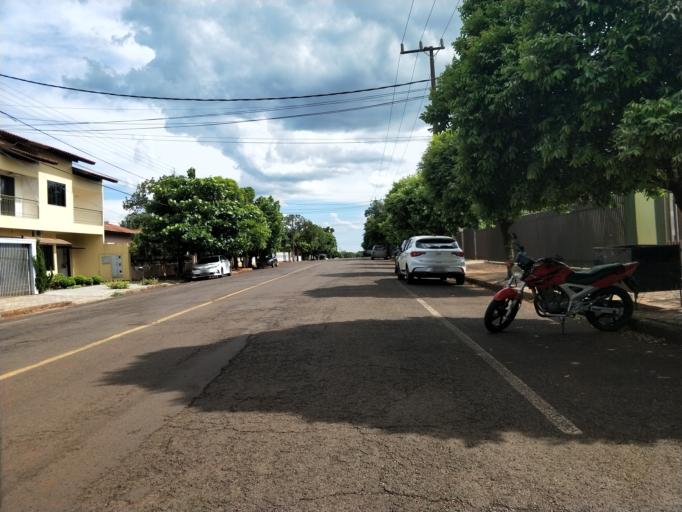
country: BR
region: Parana
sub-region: Marechal Candido Rondon
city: Marechal Candido Rondon
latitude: -24.5602
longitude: -54.0542
